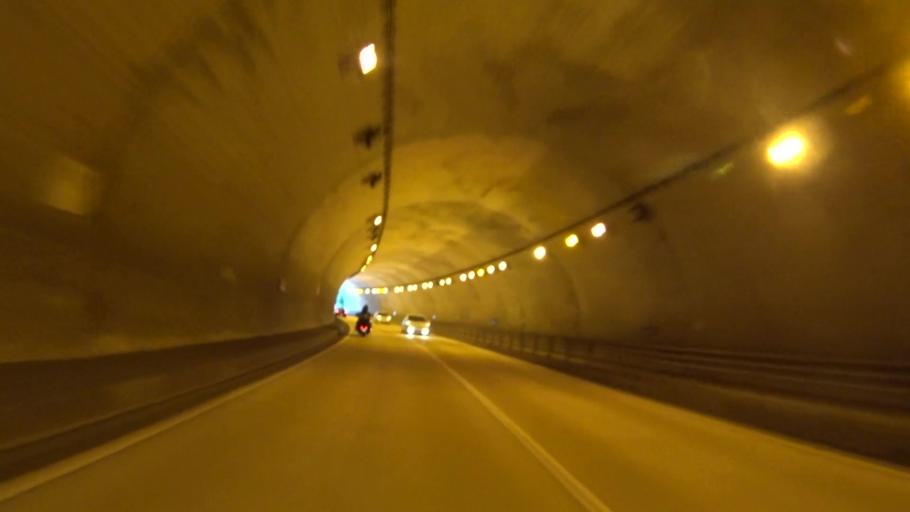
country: JP
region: Hyogo
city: Sasayama
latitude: 35.0696
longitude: 135.3842
